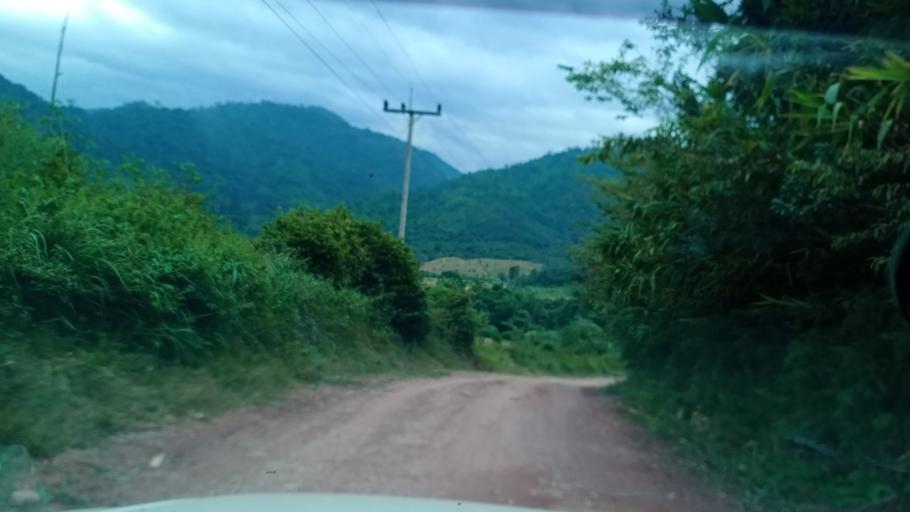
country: TH
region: Changwat Bueng Kan
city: Pak Khat
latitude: 18.7199
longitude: 103.2270
